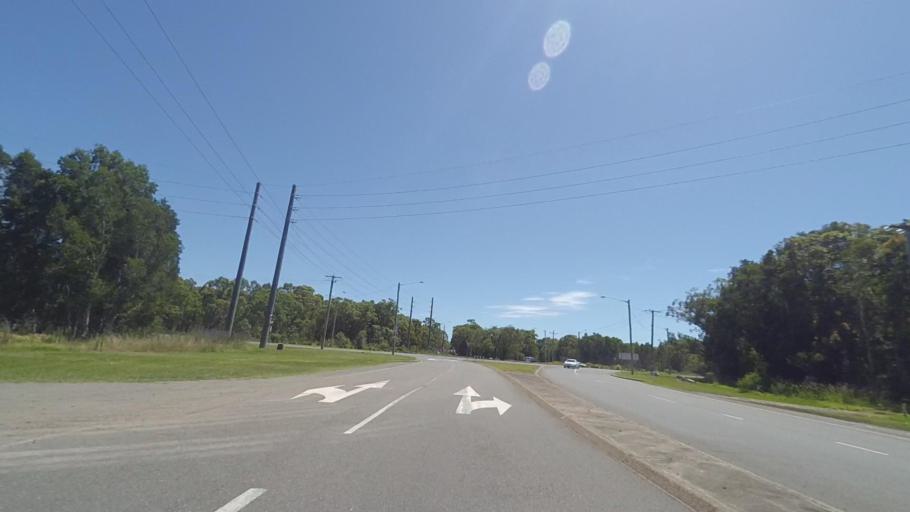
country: AU
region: New South Wales
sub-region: Port Stephens Shire
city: Medowie
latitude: -32.7729
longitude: 151.8595
